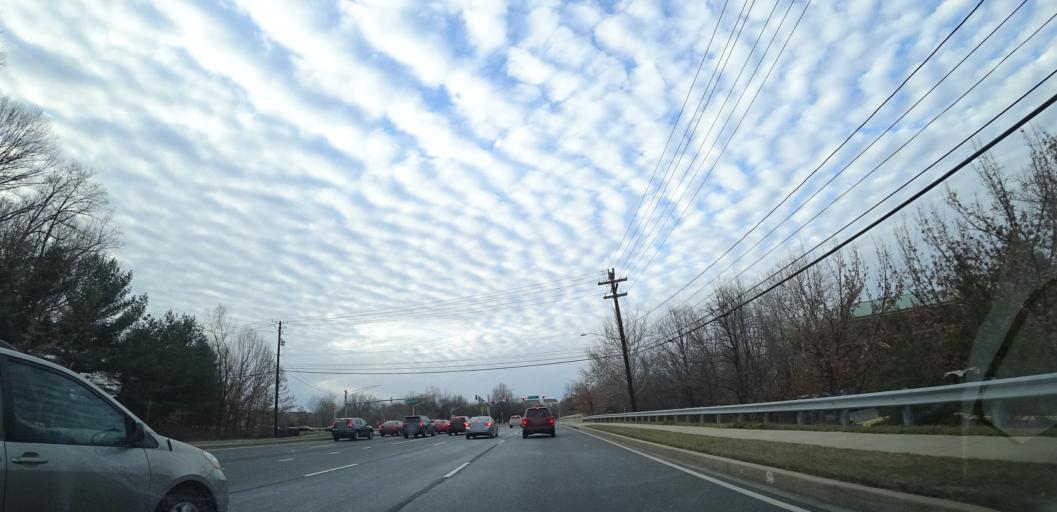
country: US
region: Maryland
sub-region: Montgomery County
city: Rockville
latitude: 39.0925
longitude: -77.1818
